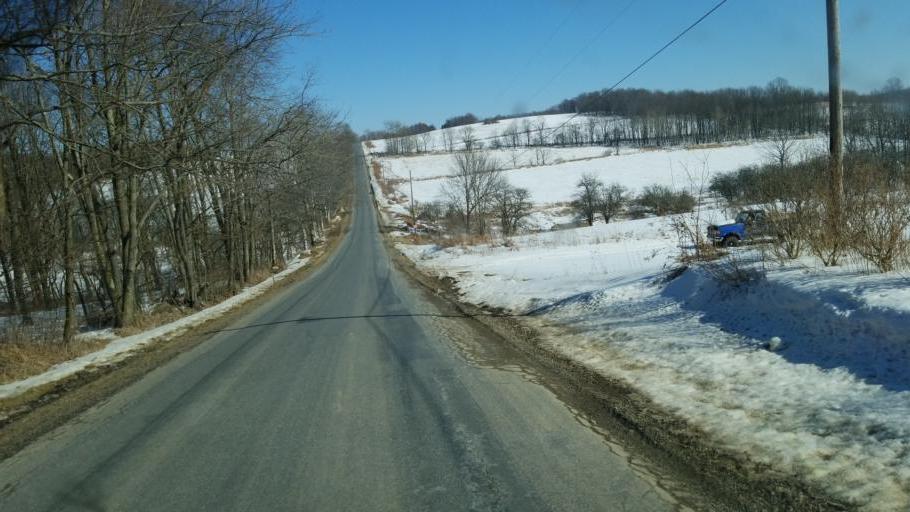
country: US
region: Pennsylvania
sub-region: Tioga County
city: Westfield
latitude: 41.9948
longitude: -77.6715
